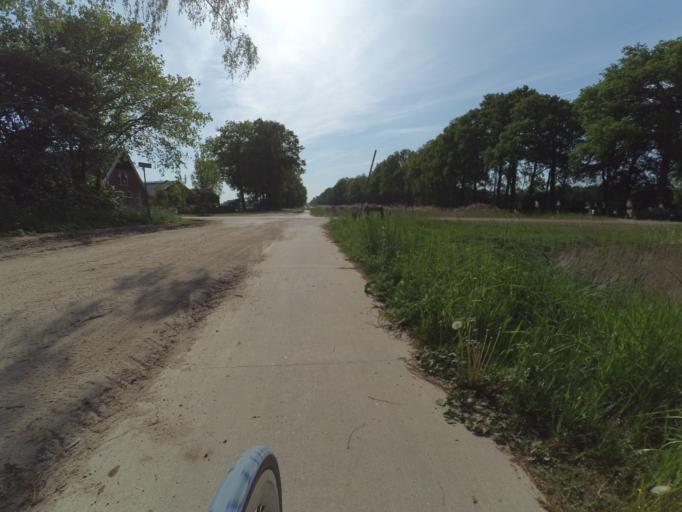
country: NL
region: Overijssel
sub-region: Gemeente Oldenzaal
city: Oldenzaal
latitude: 52.3764
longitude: 6.8800
